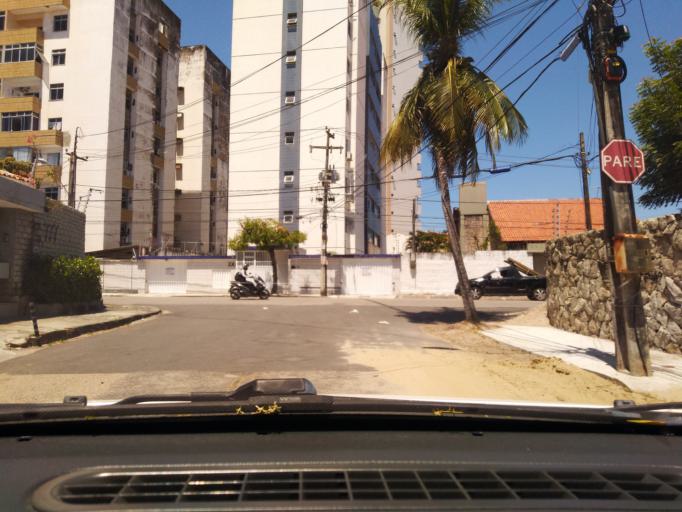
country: BR
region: Ceara
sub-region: Fortaleza
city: Fortaleza
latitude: -3.7364
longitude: -38.4720
